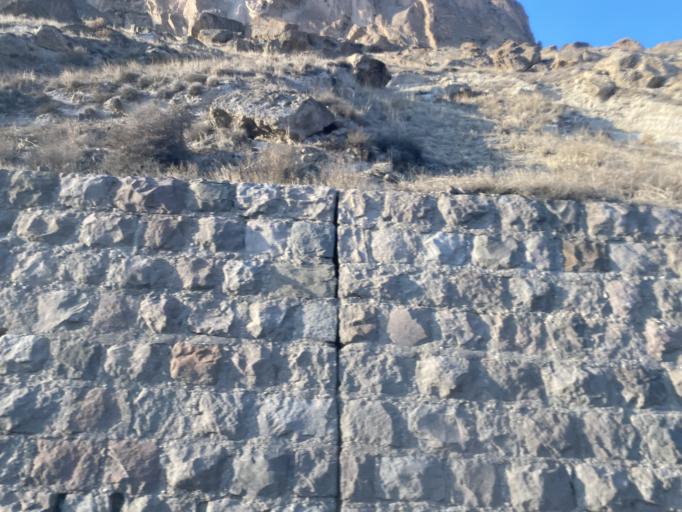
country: IR
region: Tehran
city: Damavand
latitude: 35.8911
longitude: 52.2048
